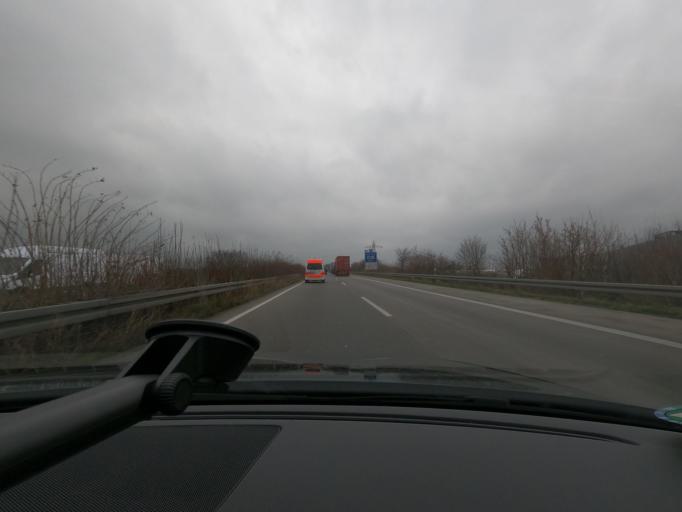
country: DE
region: North Rhine-Westphalia
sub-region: Regierungsbezirk Arnsberg
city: Bad Sassendorf
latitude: 51.5520
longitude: 8.1535
